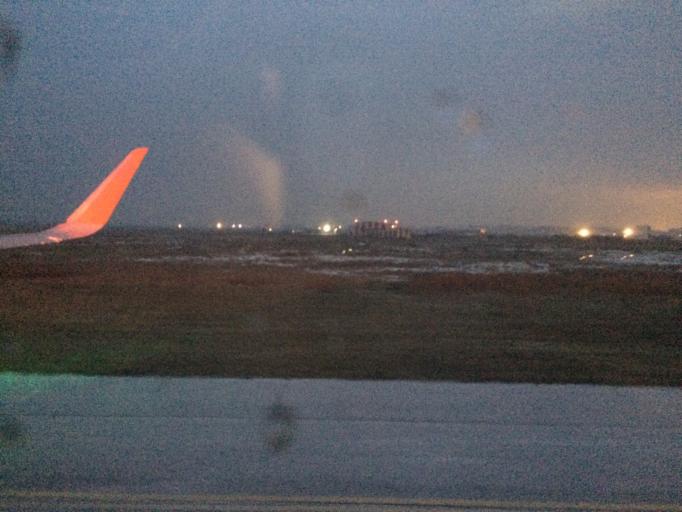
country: RU
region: Novosibirsk
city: Ob'
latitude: 55.0140
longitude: 82.6775
